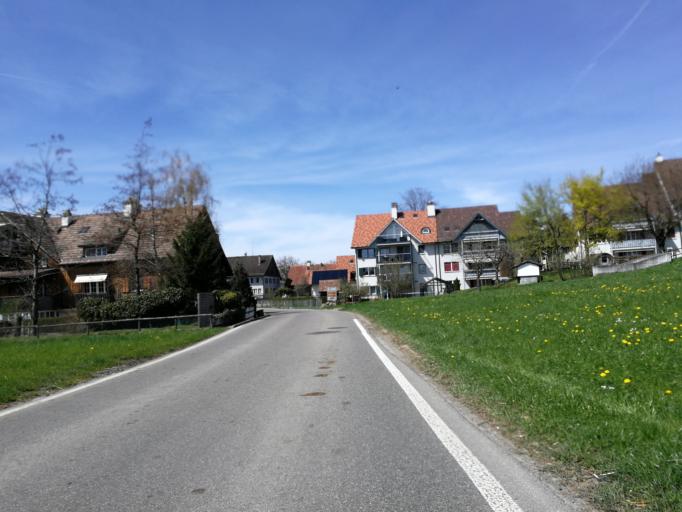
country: CH
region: Zurich
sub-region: Bezirk Meilen
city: Herrliberg
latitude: 47.2939
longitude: 8.6323
